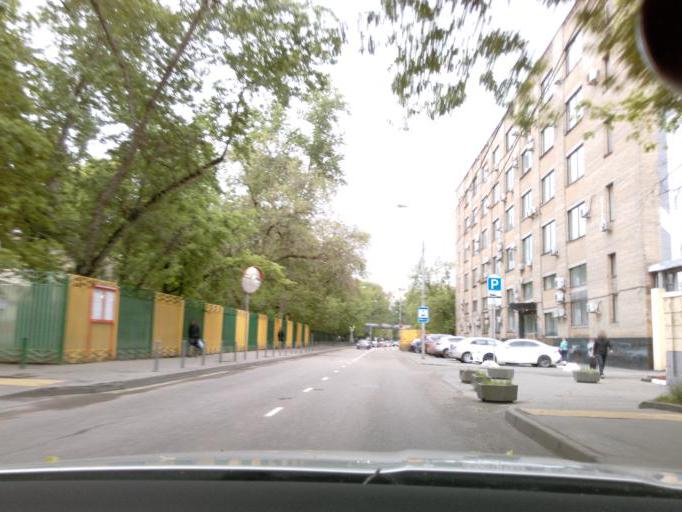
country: RU
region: Moskovskaya
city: Dorogomilovo
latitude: 55.7818
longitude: 37.5842
